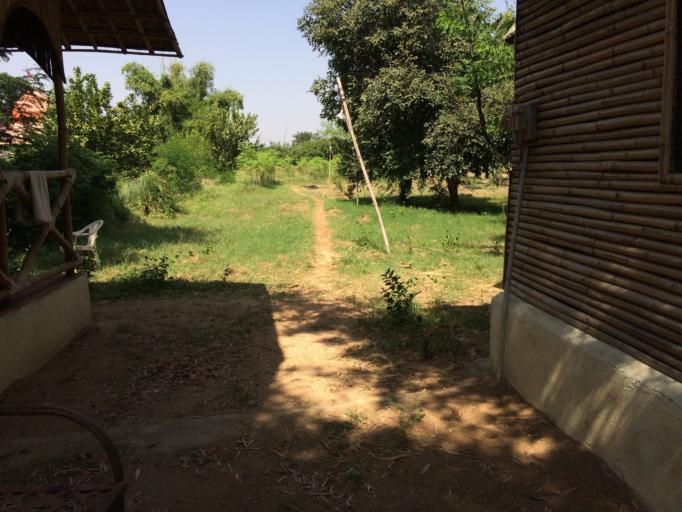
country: IN
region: Madhya Pradesh
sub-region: Dewas
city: Khategaon
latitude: 22.4947
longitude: 76.9316
